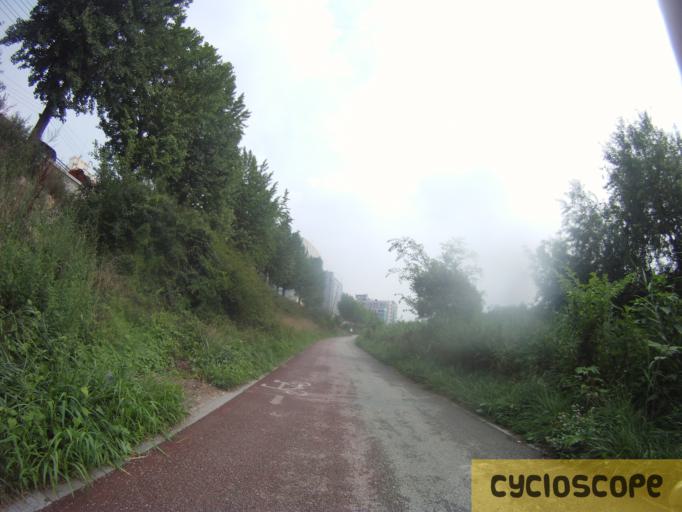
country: KR
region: Gyeonggi-do
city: Anyang-si
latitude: 37.3914
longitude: 126.9414
